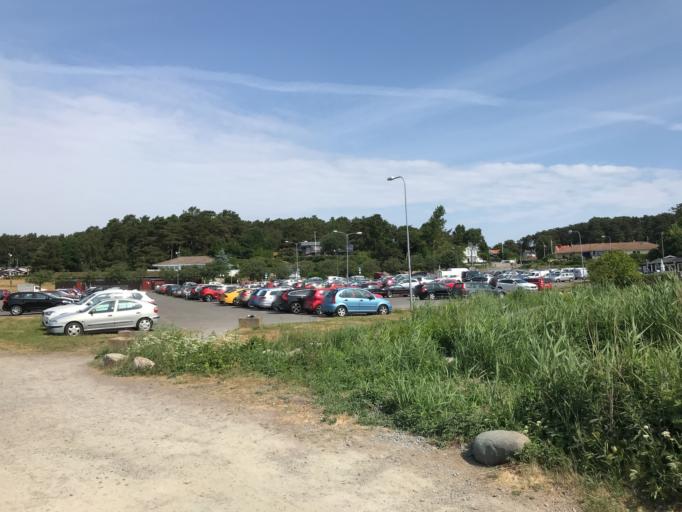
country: SE
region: Vaestra Goetaland
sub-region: Goteborg
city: Billdal
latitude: 57.6278
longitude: 11.9223
